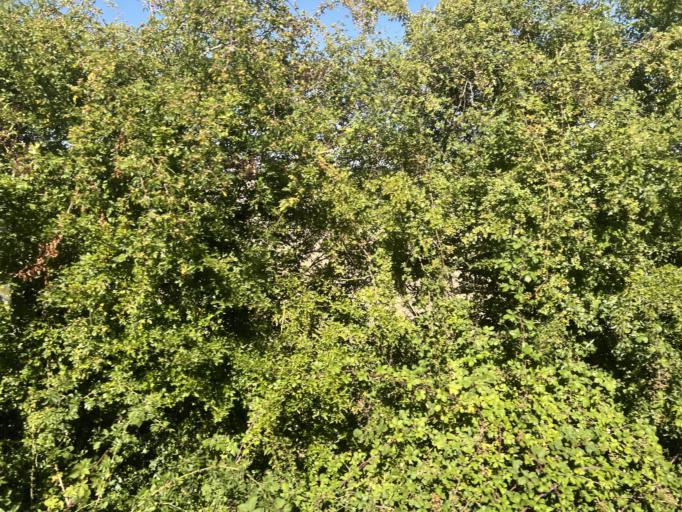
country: GB
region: England
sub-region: Lincolnshire
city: Boston
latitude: 53.0222
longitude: 0.0099
